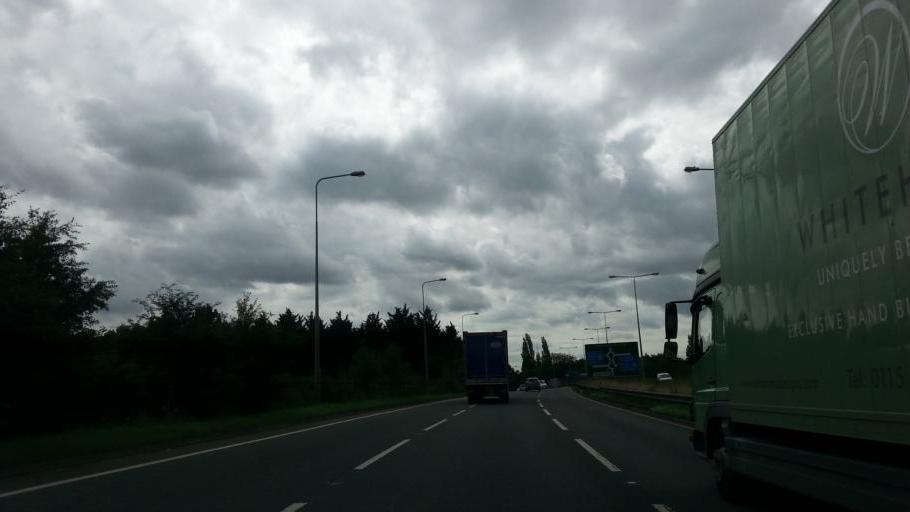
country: GB
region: England
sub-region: Northamptonshire
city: Hardingstone
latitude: 52.1911
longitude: -0.8929
